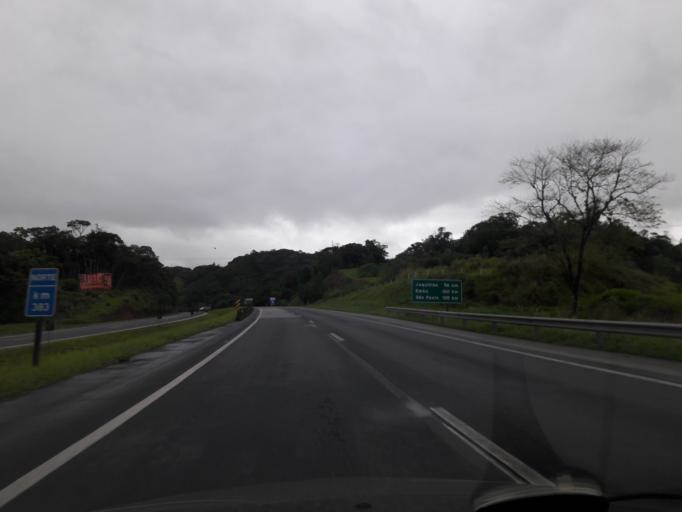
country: BR
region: Sao Paulo
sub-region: Miracatu
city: Miracatu
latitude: -24.2424
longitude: -47.3641
